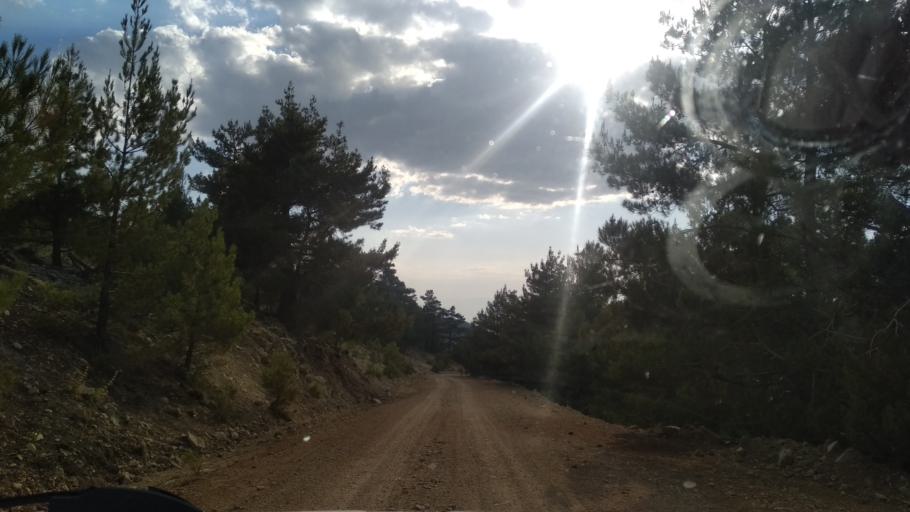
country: TR
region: Mersin
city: Sarikavak
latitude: 36.6006
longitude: 33.7177
